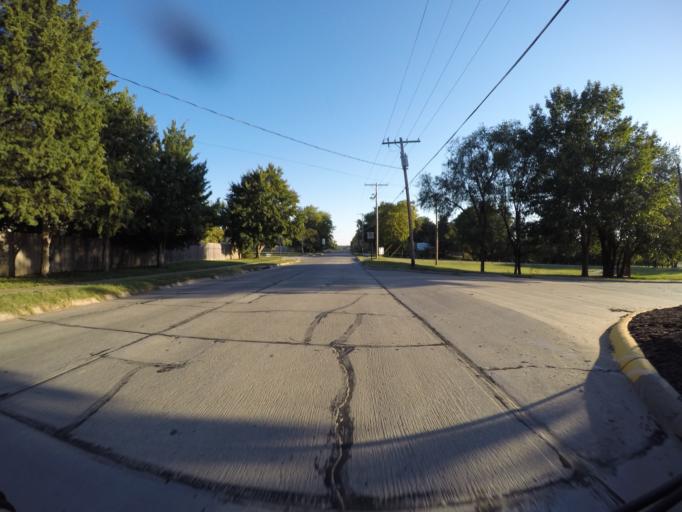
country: US
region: Kansas
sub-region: Riley County
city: Manhattan
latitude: 39.1942
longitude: -96.6260
